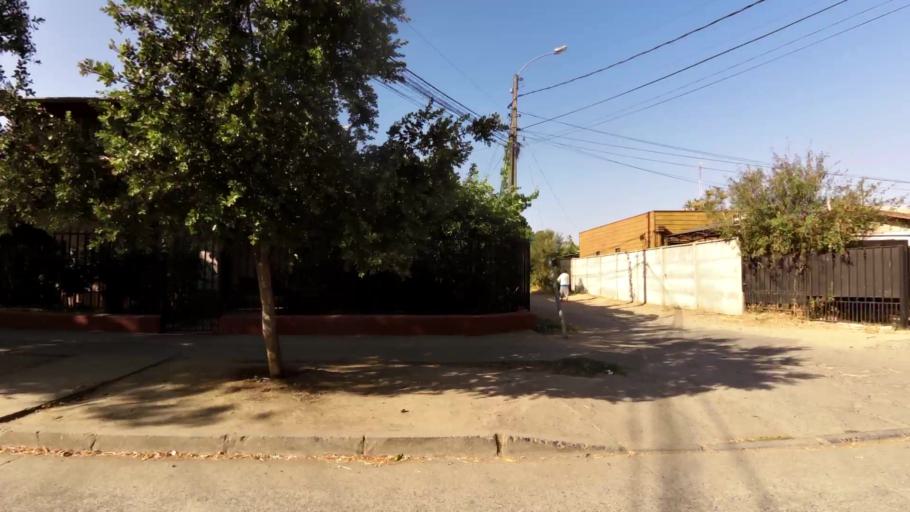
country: CL
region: Maule
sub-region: Provincia de Talca
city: Talca
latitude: -35.4181
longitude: -71.6699
